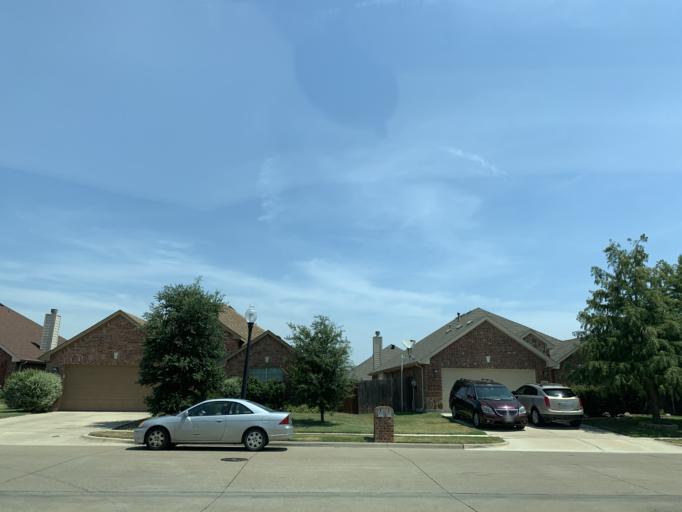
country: US
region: Texas
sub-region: Dallas County
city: Cedar Hill
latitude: 32.6453
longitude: -97.0400
